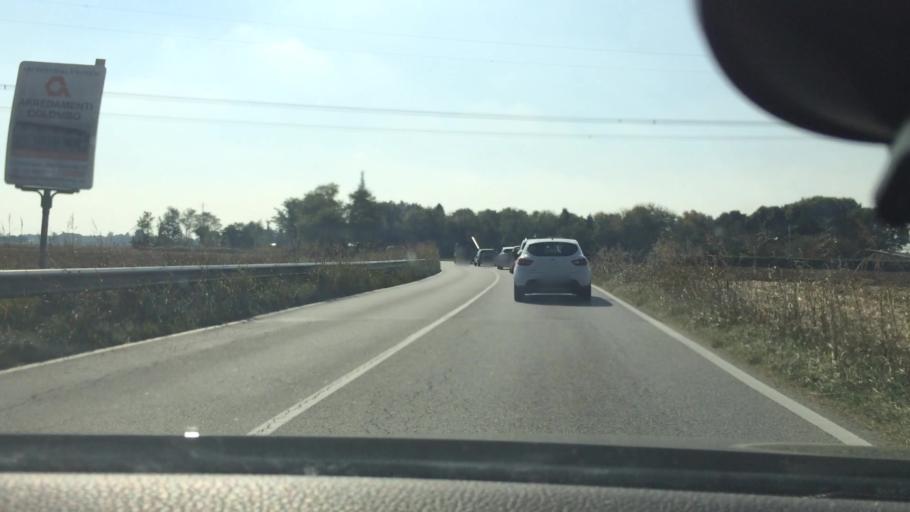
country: IT
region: Lombardy
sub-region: Citta metropolitana di Milano
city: Arconate
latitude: 45.5282
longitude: 8.8649
